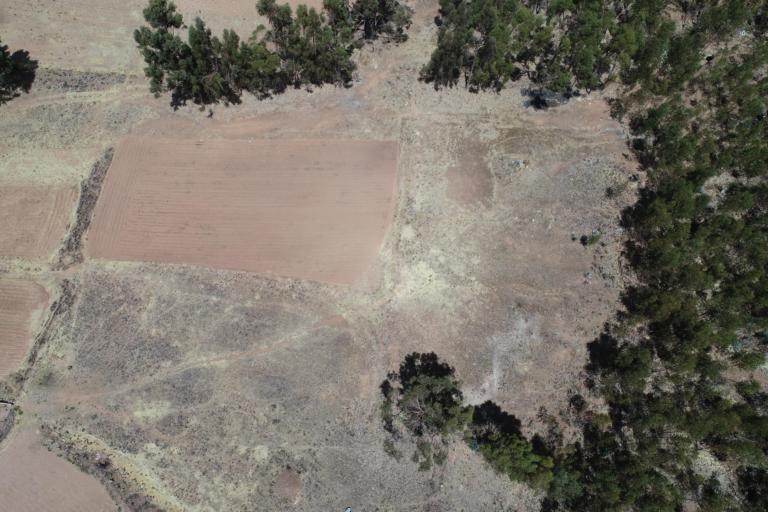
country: BO
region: La Paz
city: Achacachi
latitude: -15.9092
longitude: -68.8865
